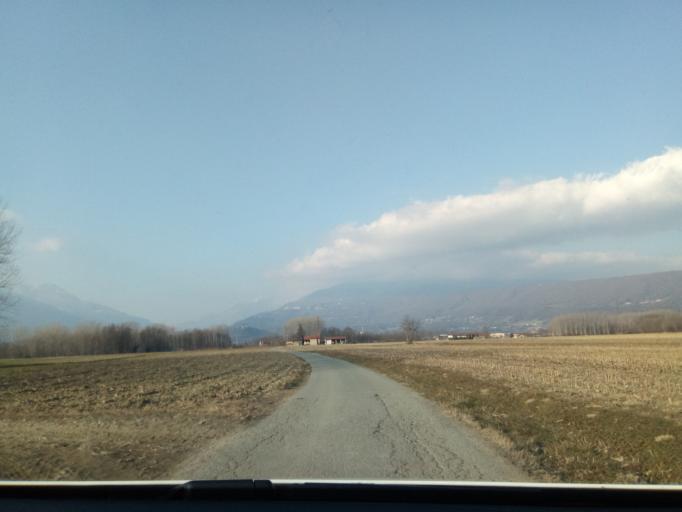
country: IT
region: Piedmont
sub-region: Provincia di Torino
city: Bollengo
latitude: 45.4546
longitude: 7.9228
